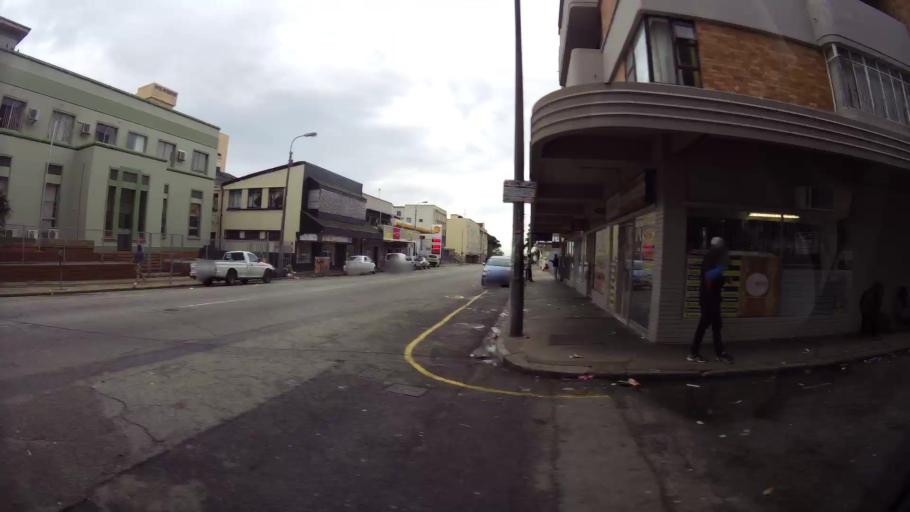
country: ZA
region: Eastern Cape
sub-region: Nelson Mandela Bay Metropolitan Municipality
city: Port Elizabeth
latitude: -33.9637
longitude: 25.6177
